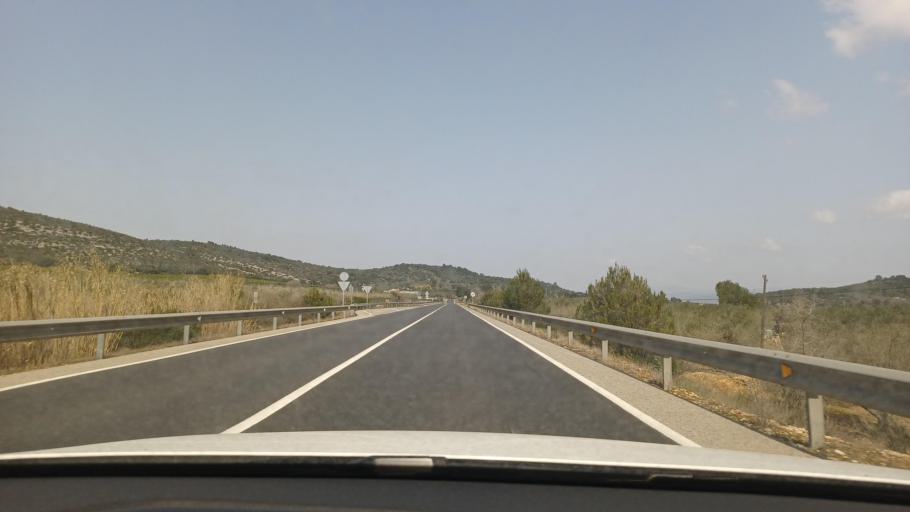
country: ES
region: Catalonia
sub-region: Provincia de Tarragona
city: Santa Barbara
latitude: 40.6619
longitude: 0.5078
